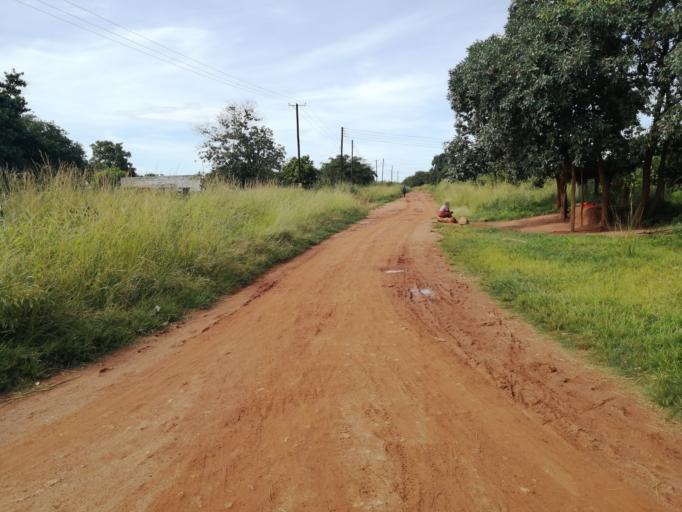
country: ZM
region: Central
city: Chibombo
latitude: -14.9026
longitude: 27.7747
